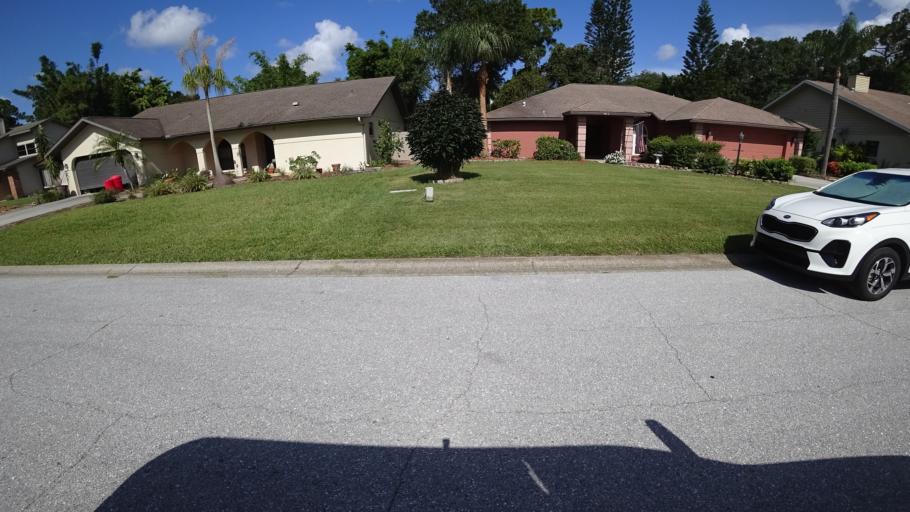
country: US
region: Florida
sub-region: Sarasota County
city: Desoto Lakes
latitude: 27.3990
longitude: -82.5000
